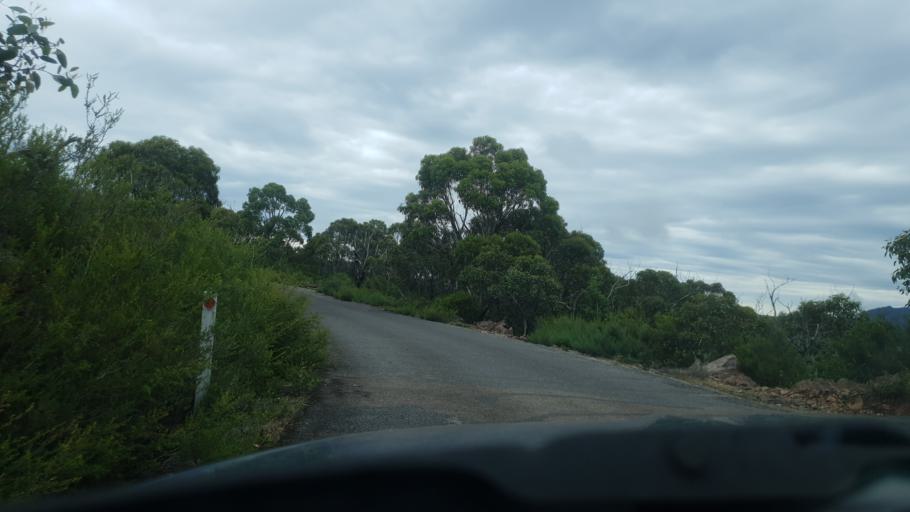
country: AU
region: Victoria
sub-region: Northern Grampians
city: Stawell
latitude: -37.2657
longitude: 142.5772
